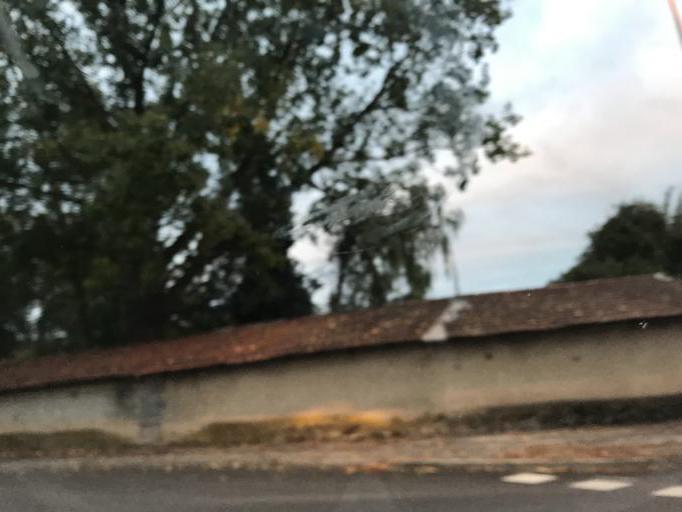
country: FR
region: Rhone-Alpes
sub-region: Departement de l'Ain
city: Saint-Didier-de-Formans
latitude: 45.9370
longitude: 4.7861
